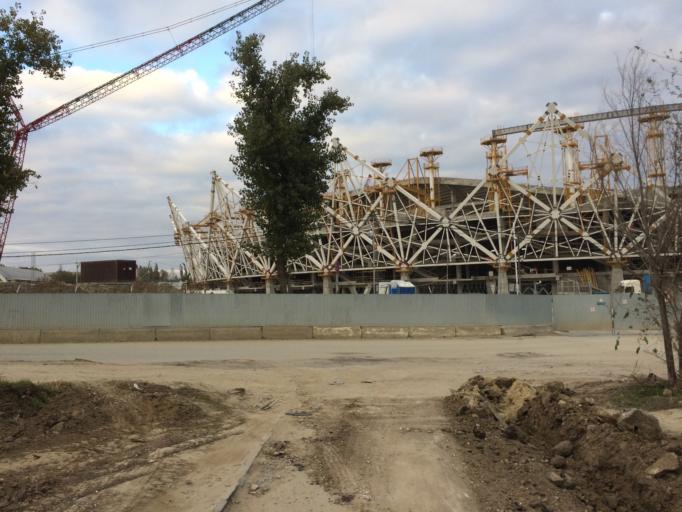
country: RU
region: Volgograd
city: Krasnoslobodsk
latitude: 48.7331
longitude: 44.5459
